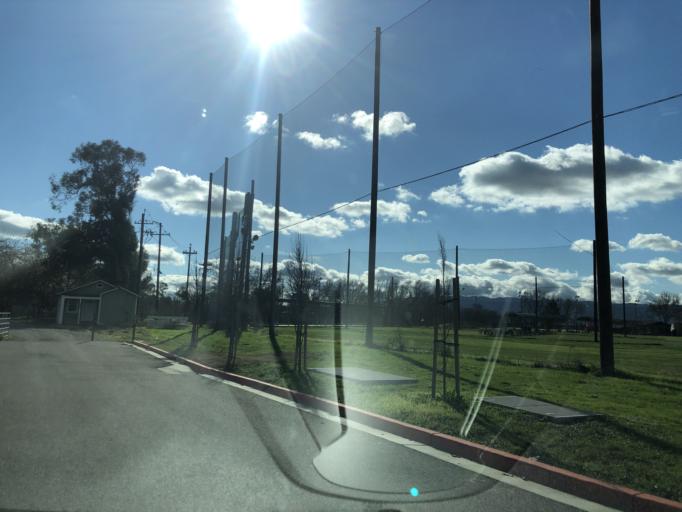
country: US
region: California
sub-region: Alameda County
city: Pleasanton
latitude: 37.6989
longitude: -121.8343
